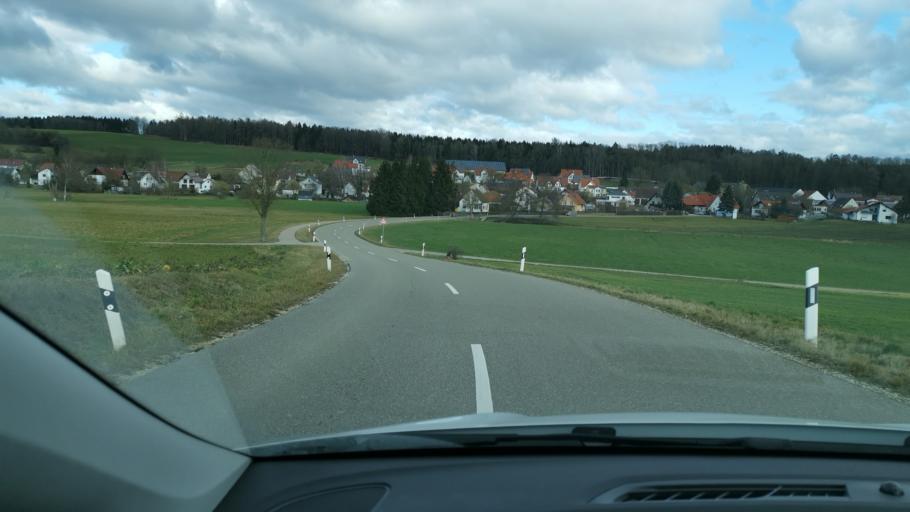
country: DE
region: Bavaria
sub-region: Swabia
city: Aindling
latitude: 48.5292
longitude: 10.9580
